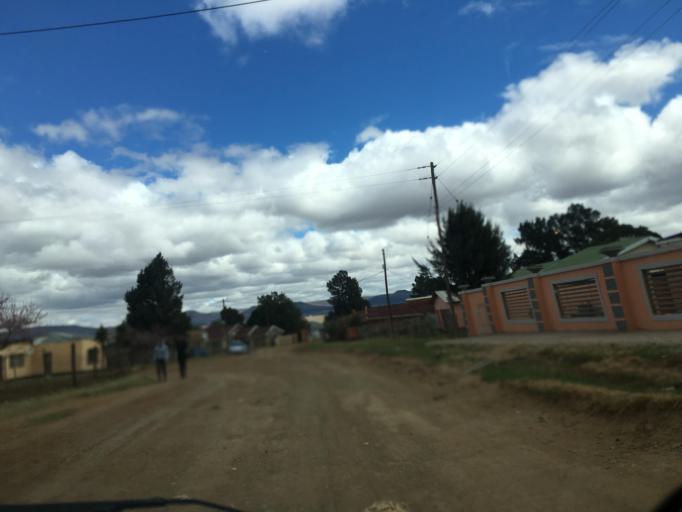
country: ZA
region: Eastern Cape
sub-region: Chris Hani District Municipality
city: Cala
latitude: -31.5314
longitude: 27.6967
